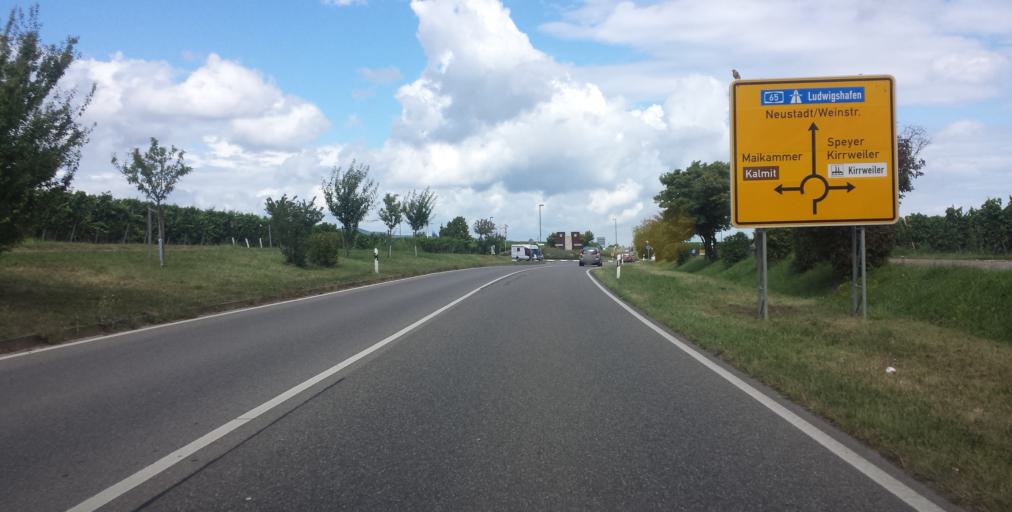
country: DE
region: Rheinland-Pfalz
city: Maikammer
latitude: 49.3049
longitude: 8.1422
